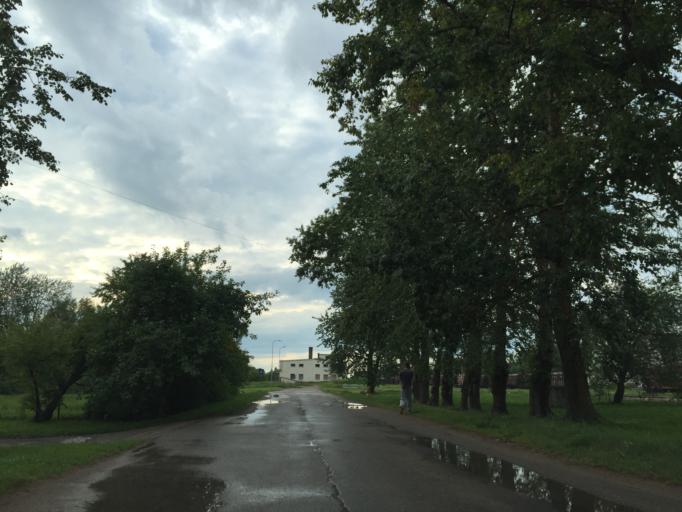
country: LV
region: Dobeles Rajons
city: Dobele
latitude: 56.6292
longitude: 23.2833
